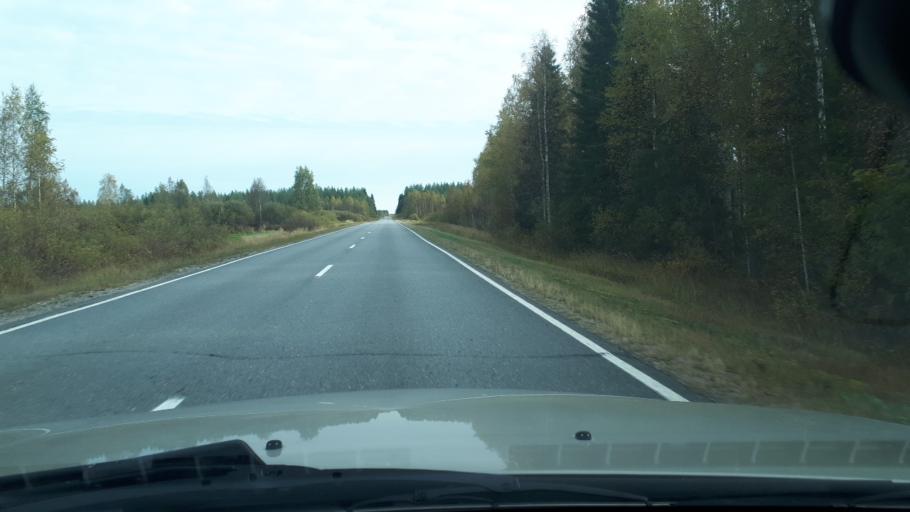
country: FI
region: Lapland
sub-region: Rovaniemi
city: Ranua
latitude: 65.9639
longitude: 26.0785
